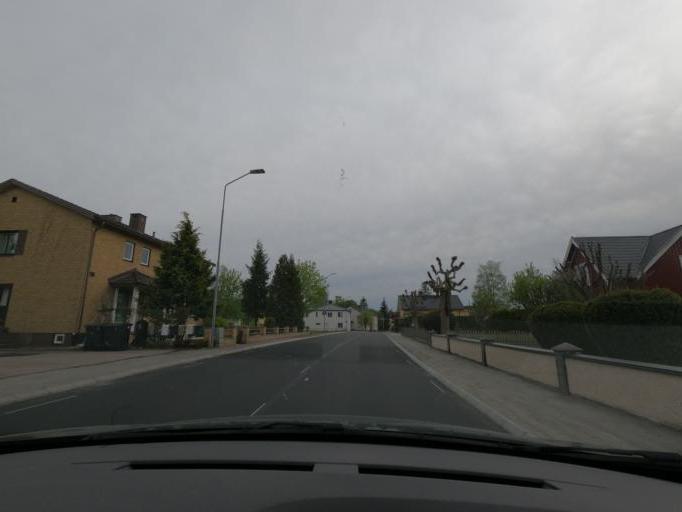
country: SE
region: Joenkoeping
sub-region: Varnamo Kommun
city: Bredaryd
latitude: 57.2213
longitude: 13.7837
